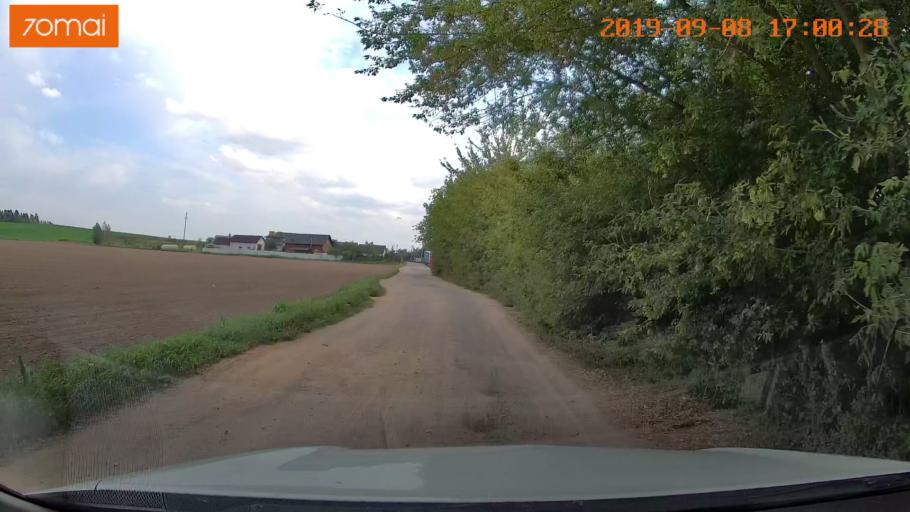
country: BY
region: Grodnenskaya
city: Hrodna
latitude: 53.7151
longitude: 23.9325
